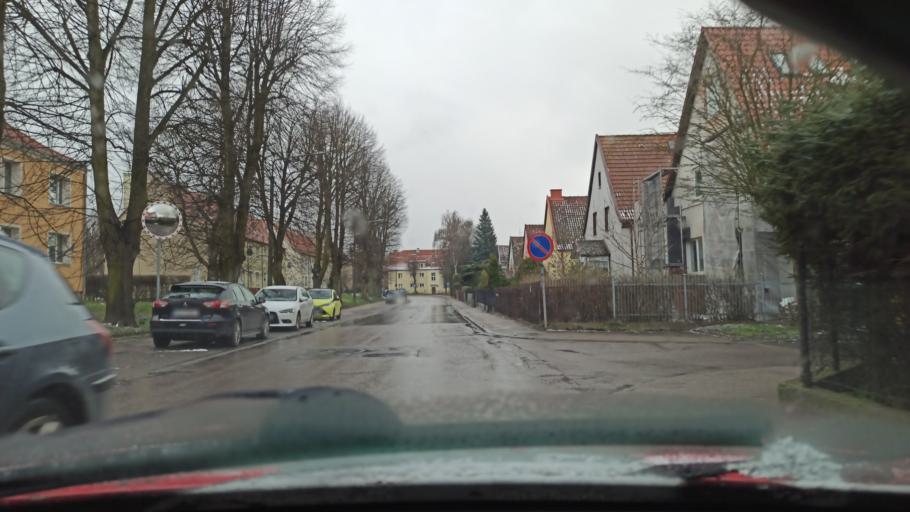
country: PL
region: Warmian-Masurian Voivodeship
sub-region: Powiat elblaski
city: Elblag
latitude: 54.1750
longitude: 19.4127
